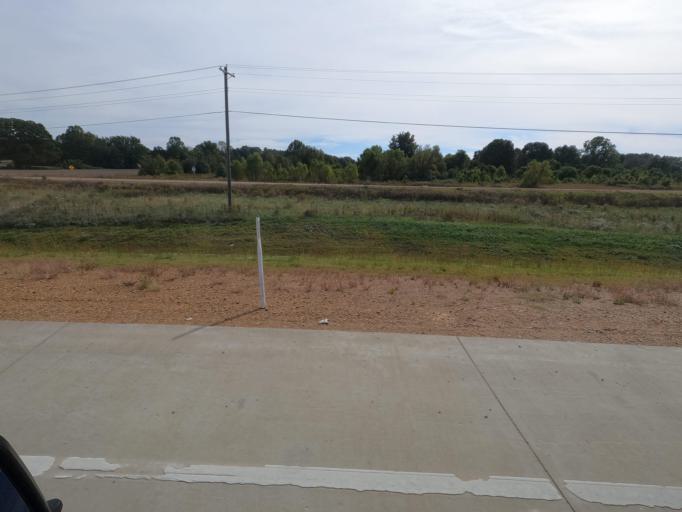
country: US
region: Tennessee
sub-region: Fayette County
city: Hickory Withe
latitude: 35.2901
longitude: -89.6096
